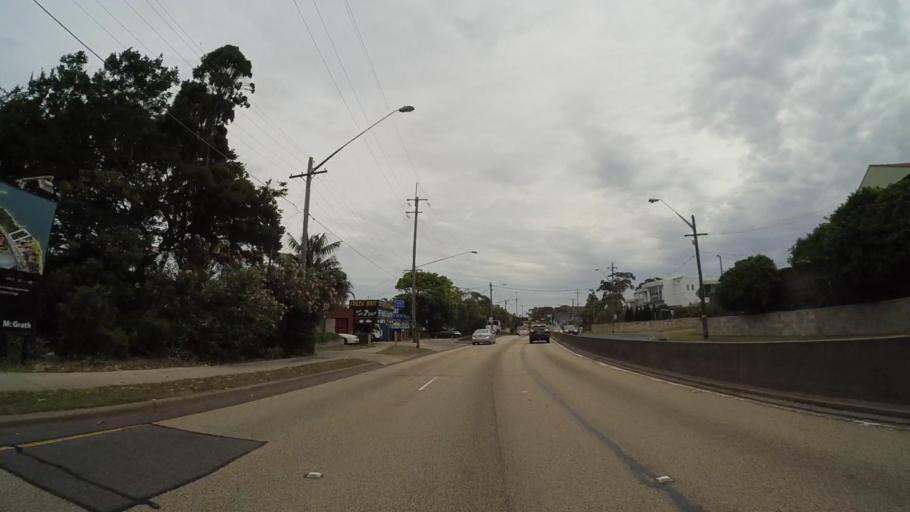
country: AU
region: New South Wales
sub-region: Kogarah
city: Blakehurst
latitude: -33.9960
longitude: 151.1169
